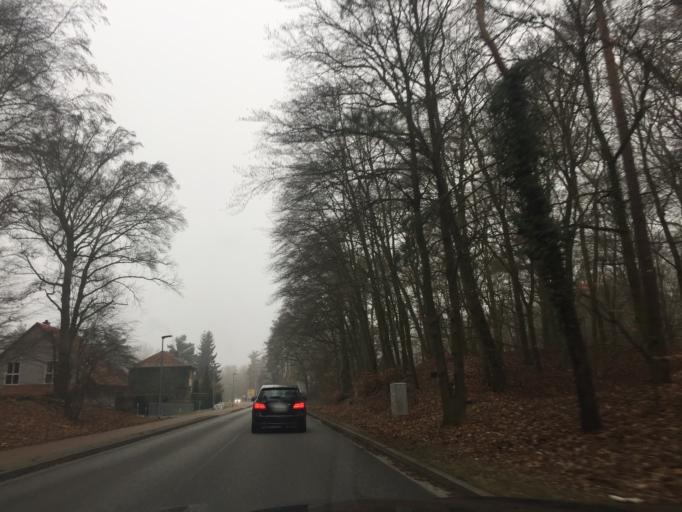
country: DE
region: Brandenburg
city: Falkensee
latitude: 52.6007
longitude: 13.1046
